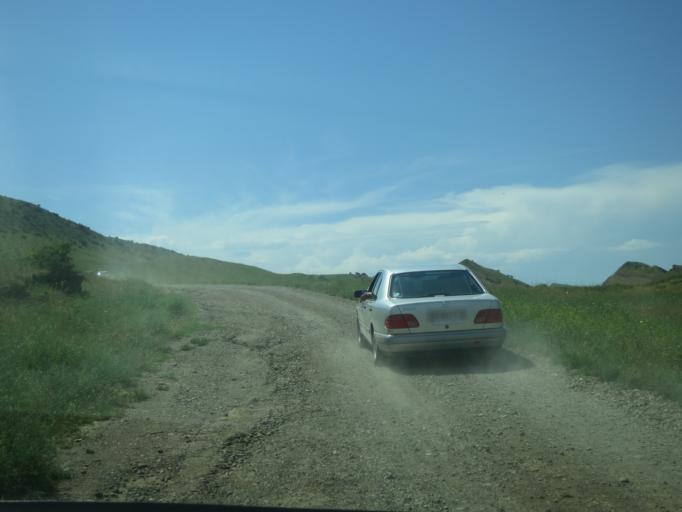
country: AZ
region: Agstafa
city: Saloglu
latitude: 41.4597
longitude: 45.3537
